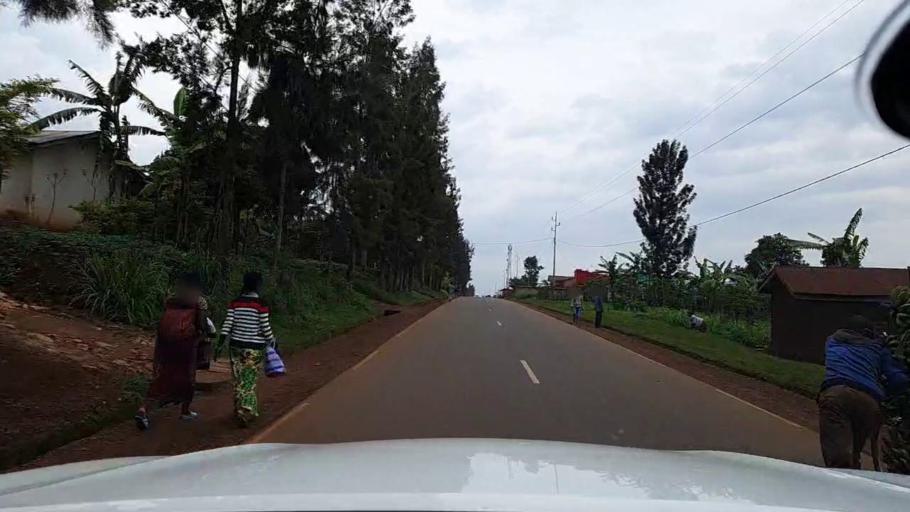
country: RW
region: Western Province
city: Cyangugu
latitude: -2.6237
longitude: 28.9479
